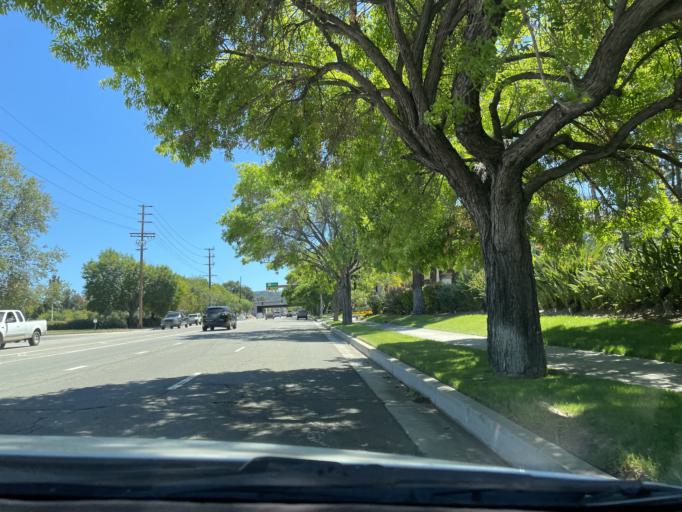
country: US
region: California
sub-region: Los Angeles County
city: Woodland Hills
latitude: 34.1720
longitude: -118.5975
